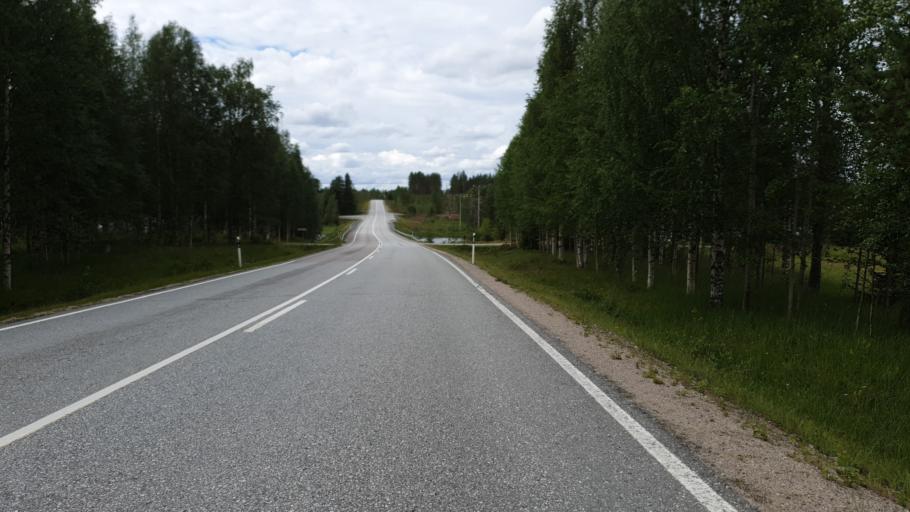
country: FI
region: Kainuu
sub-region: Kehys-Kainuu
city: Kuhmo
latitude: 64.4895
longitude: 29.8138
